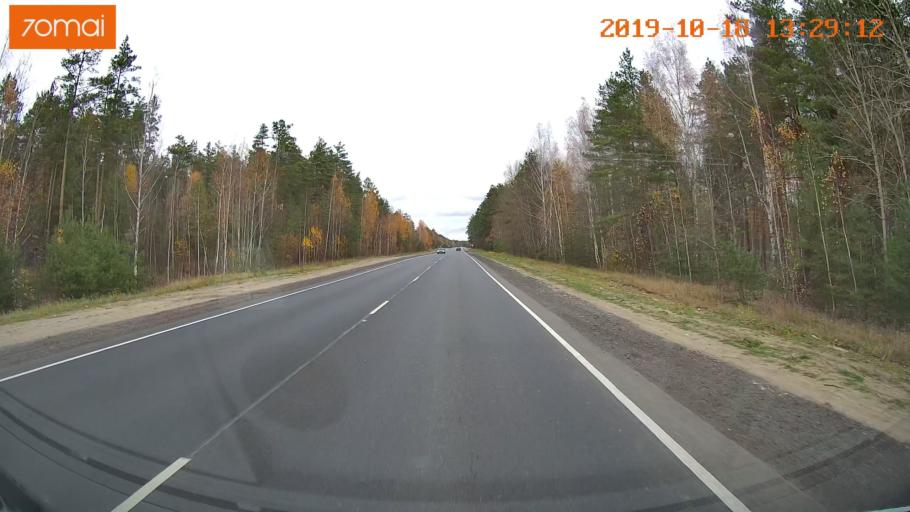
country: RU
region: Rjazan
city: Solotcha
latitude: 54.7907
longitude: 39.8732
